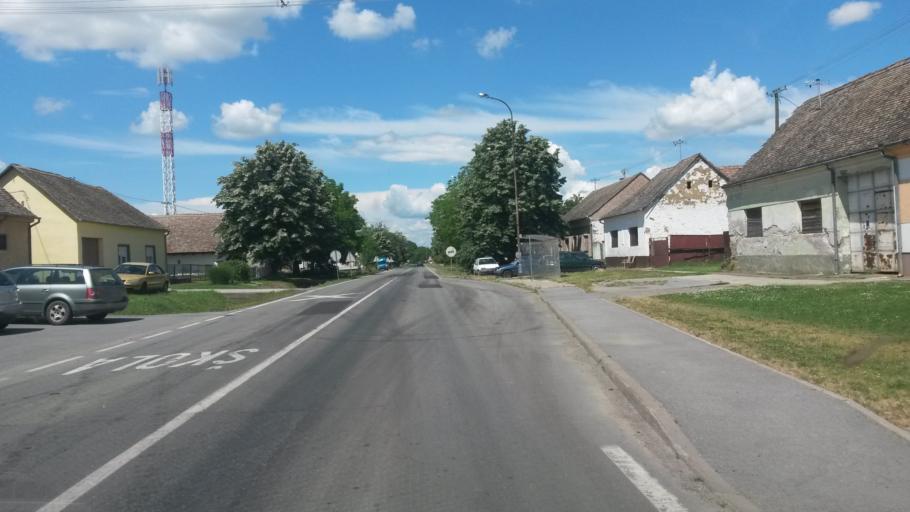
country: HR
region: Osjecko-Baranjska
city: Vuka
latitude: 45.4370
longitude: 18.5060
